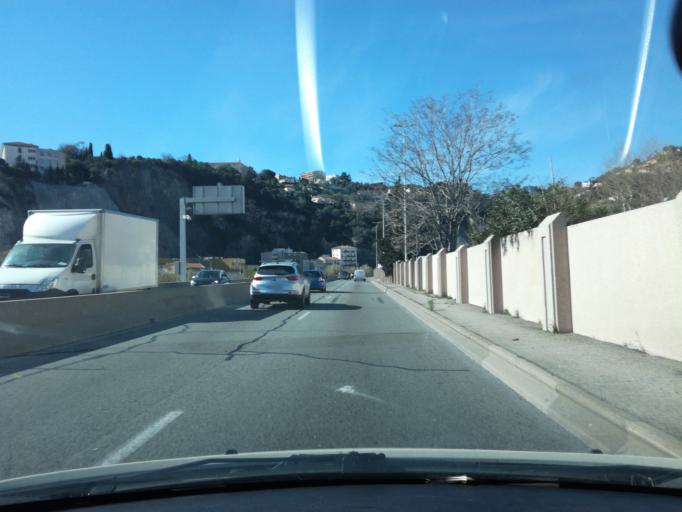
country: FR
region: Provence-Alpes-Cote d'Azur
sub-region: Departement des Alpes-Maritimes
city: Saint-Andre-de-la-Roche
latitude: 43.7261
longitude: 7.2861
